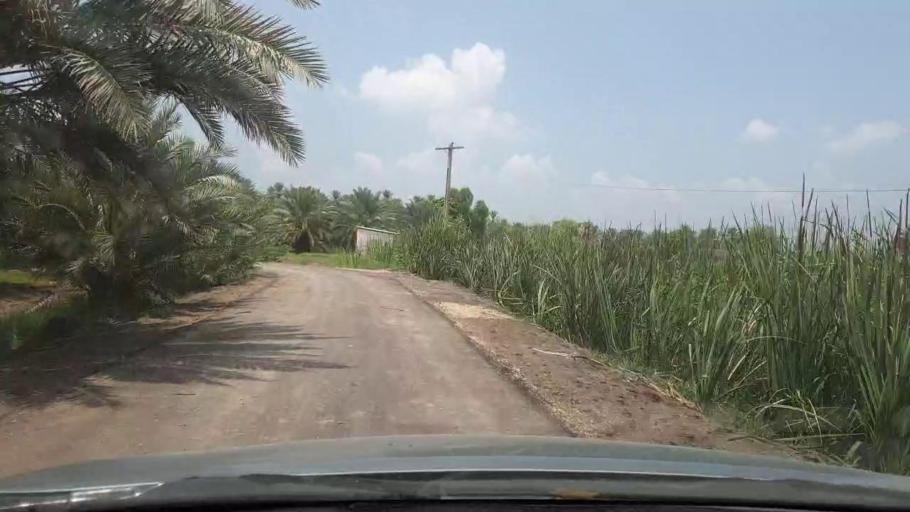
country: PK
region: Sindh
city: Khairpur
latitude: 27.4706
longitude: 68.7335
